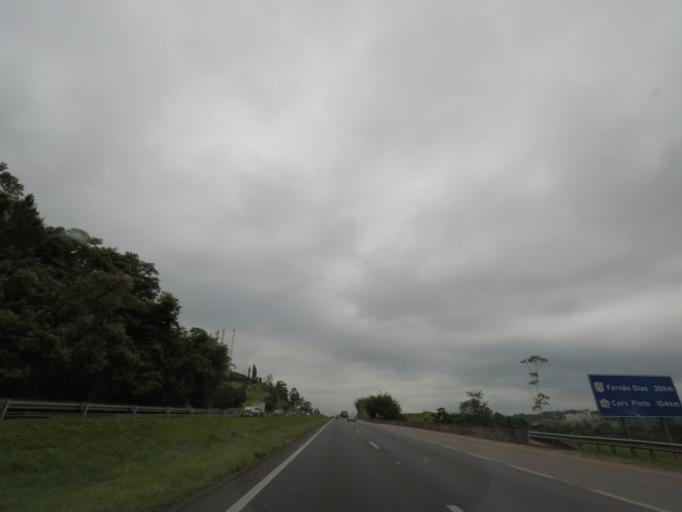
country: BR
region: Sao Paulo
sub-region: Itatiba
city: Itatiba
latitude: -22.9812
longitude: -46.8239
